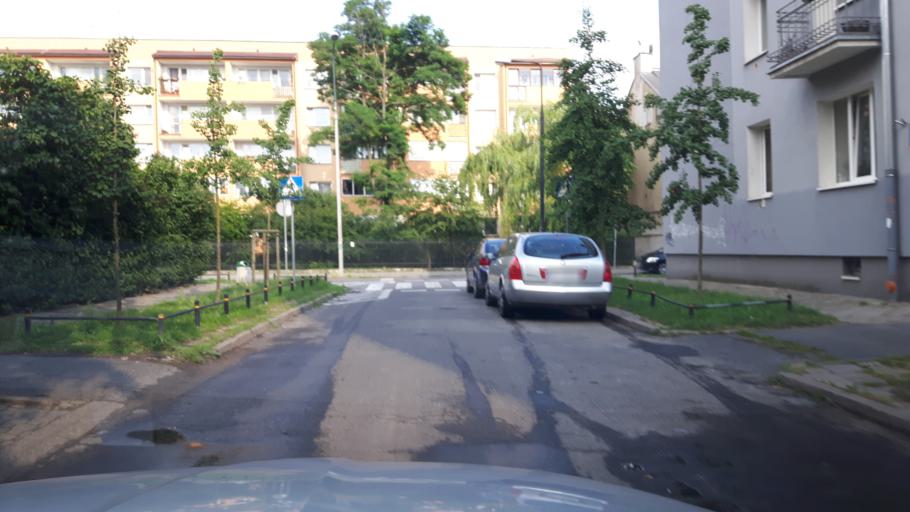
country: PL
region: Masovian Voivodeship
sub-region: Warszawa
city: Praga Poludnie
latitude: 52.2424
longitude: 21.1073
